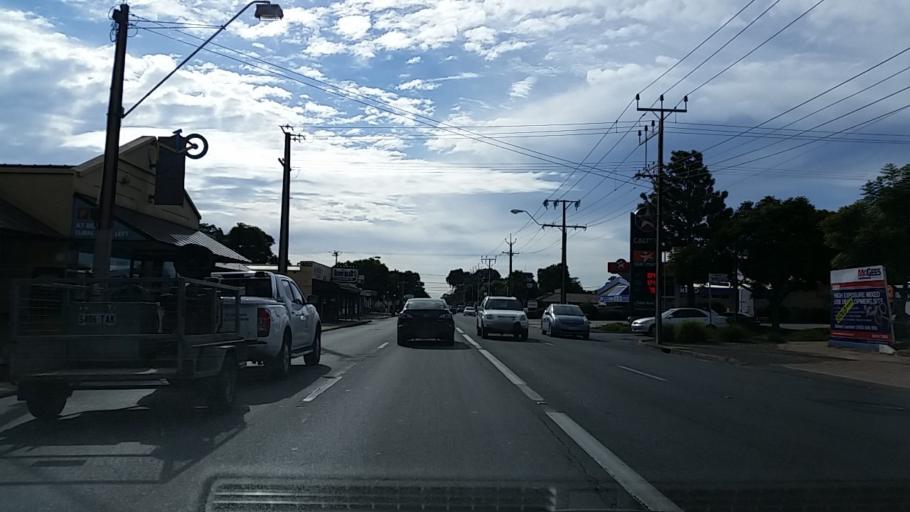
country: AU
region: South Australia
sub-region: Mitcham
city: Clarence Gardens
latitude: -34.9749
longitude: 138.5914
